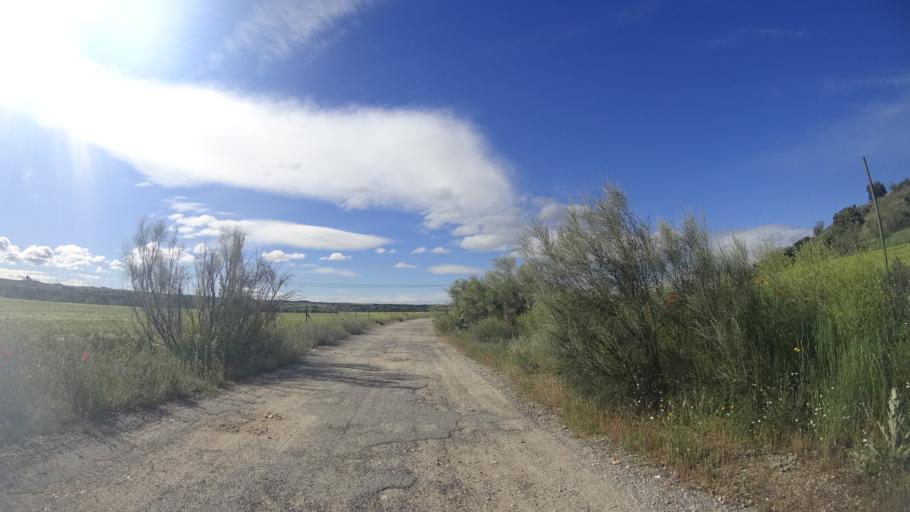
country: ES
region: Madrid
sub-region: Provincia de Madrid
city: Villanueva del Pardillo
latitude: 40.5046
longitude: -3.9395
